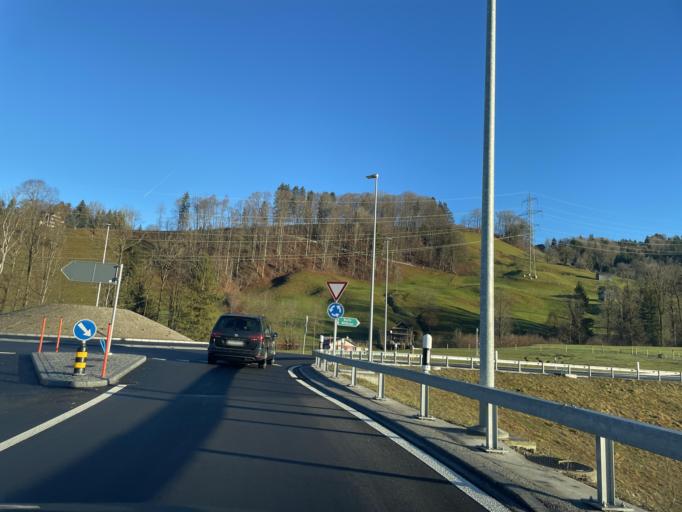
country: CH
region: Saint Gallen
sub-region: Wahlkreis Toggenburg
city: Ebnat-Kappel
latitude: 47.2761
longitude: 9.1101
